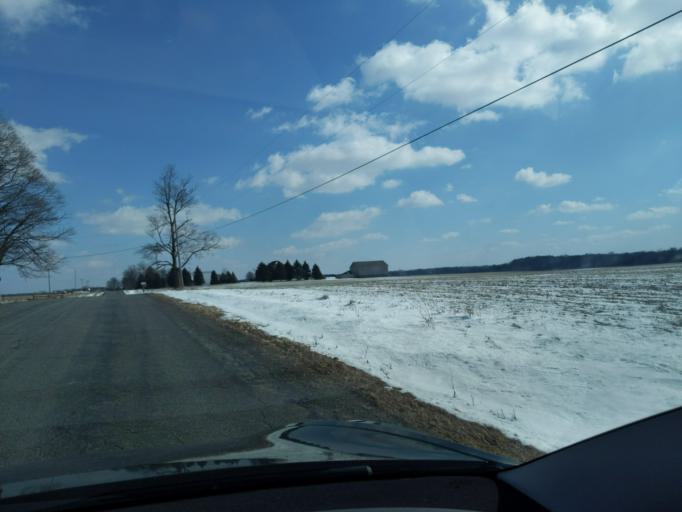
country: US
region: Michigan
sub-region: Ingham County
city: Mason
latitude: 42.6110
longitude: -84.4285
